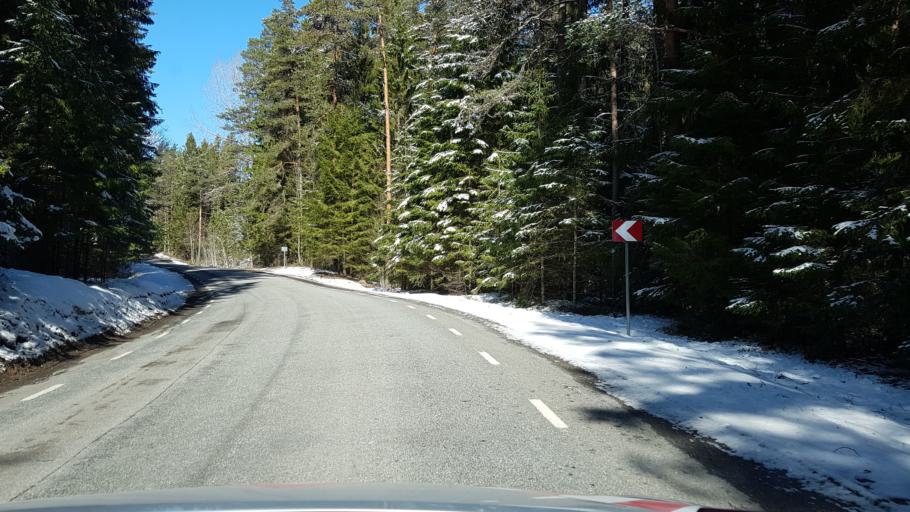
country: EE
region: Laeaene-Virumaa
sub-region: Kadrina vald
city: Kadrina
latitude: 59.4387
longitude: 26.0177
